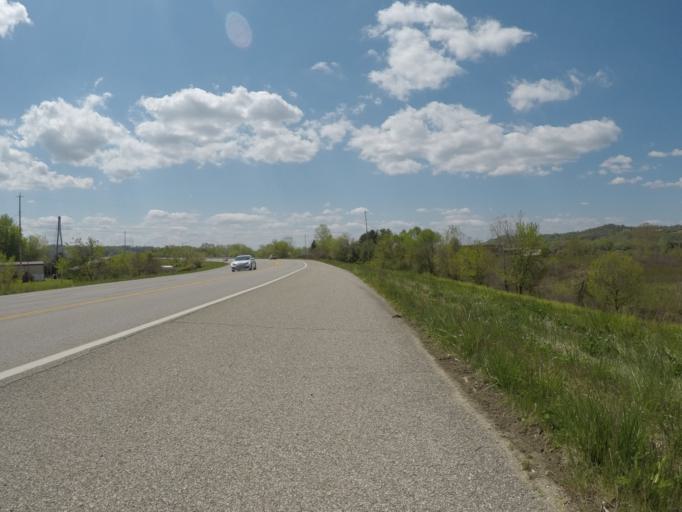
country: US
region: West Virginia
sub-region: Cabell County
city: Huntington
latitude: 38.4427
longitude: -82.3863
